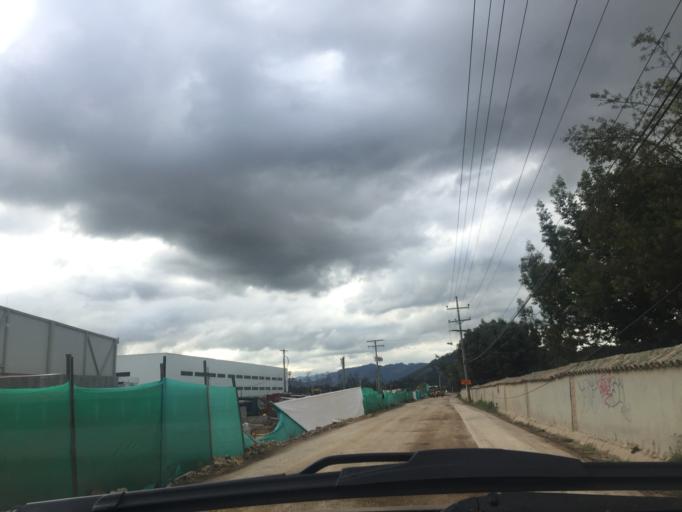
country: CO
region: Cundinamarca
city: Sopo
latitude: 4.9343
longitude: -73.9368
